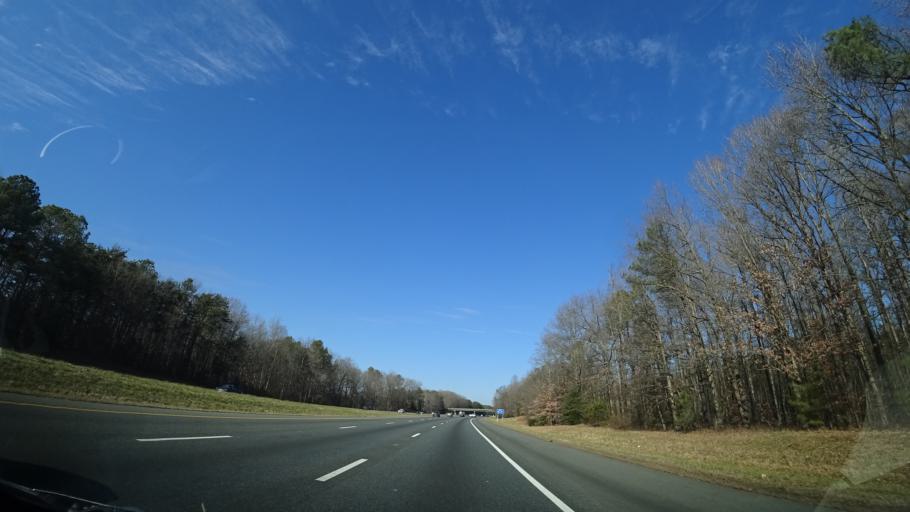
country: US
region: Virginia
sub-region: Caroline County
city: Bowling Green
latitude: 37.9692
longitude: -77.4908
